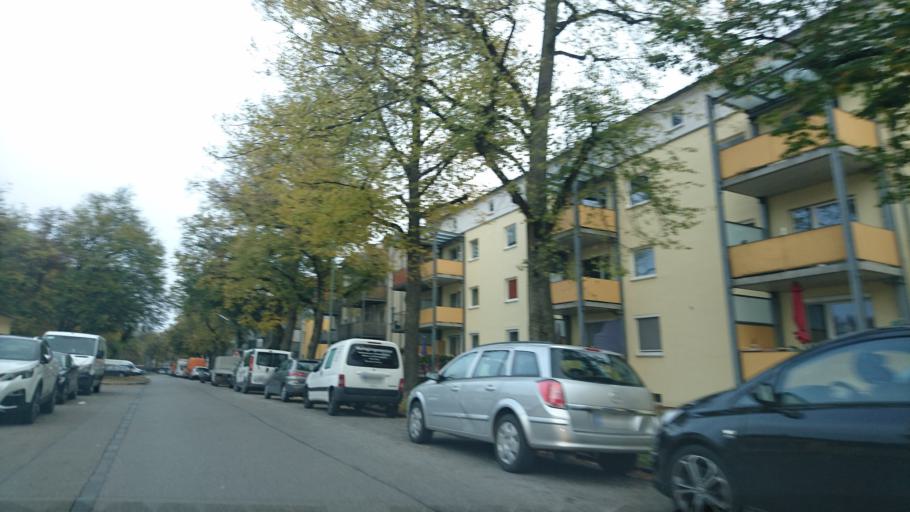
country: DE
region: Bavaria
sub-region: Swabia
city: Augsburg
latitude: 48.3936
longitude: 10.8840
